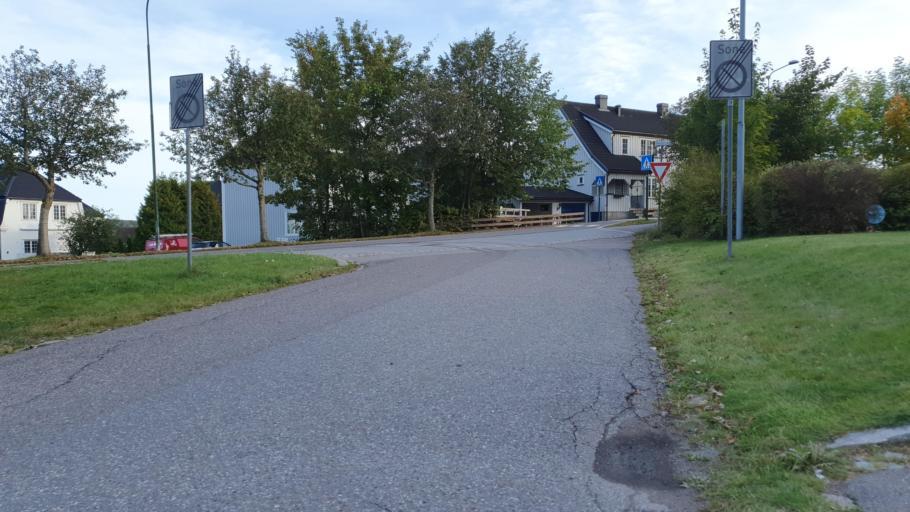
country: NO
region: Vestfold
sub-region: Tonsberg
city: Tonsberg
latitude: 59.2713
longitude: 10.4234
